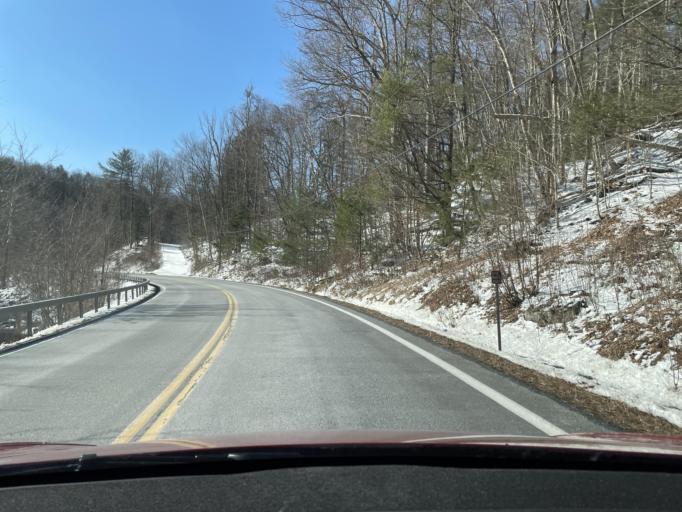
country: US
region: New York
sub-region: Ulster County
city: Shokan
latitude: 42.0600
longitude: -74.2550
